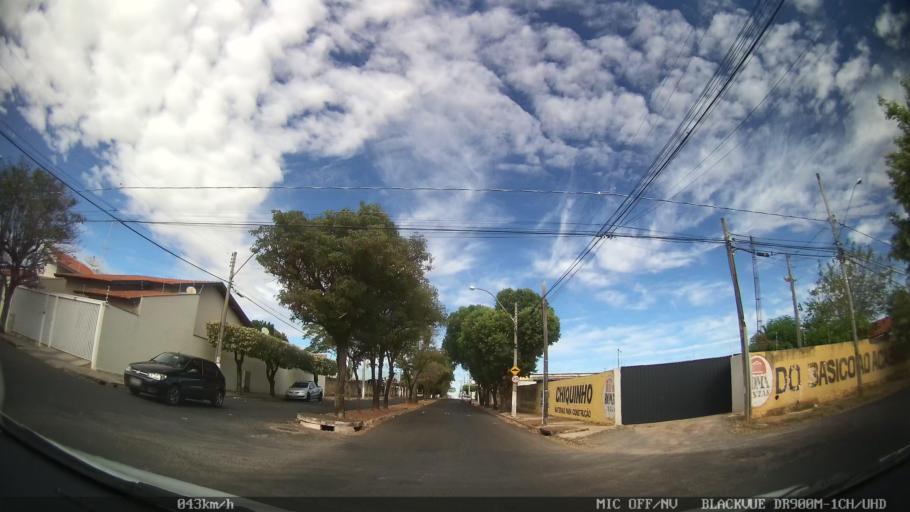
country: BR
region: Sao Paulo
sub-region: Bady Bassitt
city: Bady Bassitt
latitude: -20.8173
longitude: -49.5232
